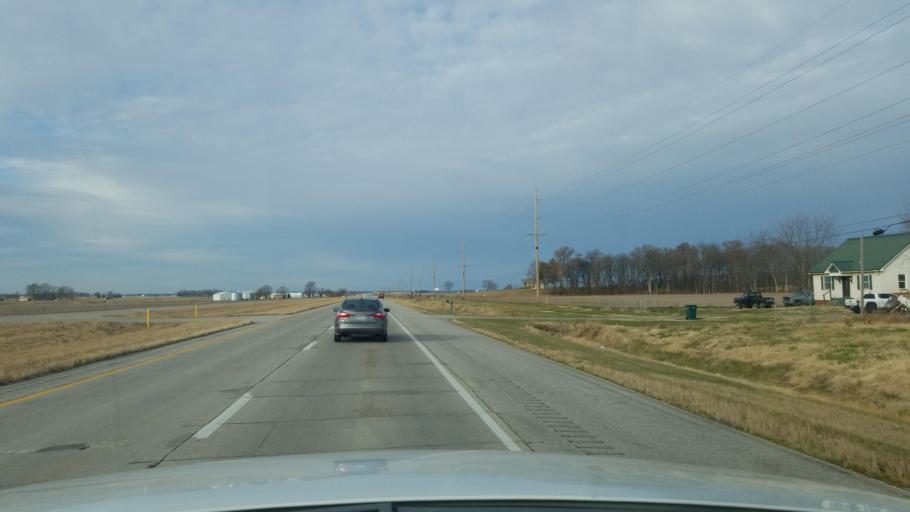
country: US
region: Indiana
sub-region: Posey County
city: Mount Vernon
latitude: 37.9422
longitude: -87.7590
